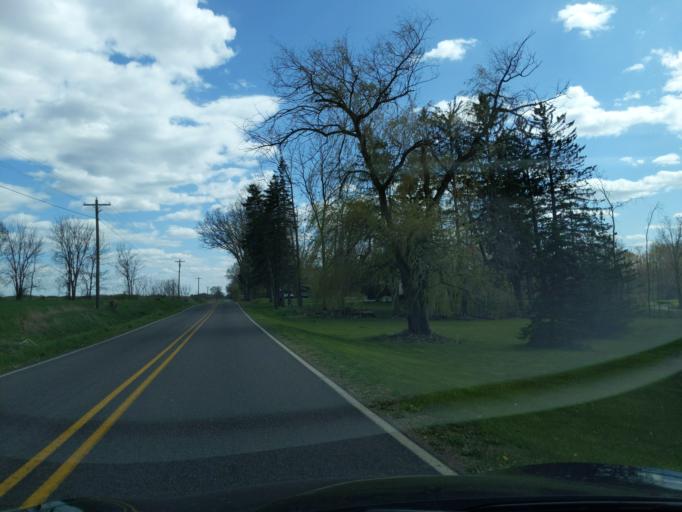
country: US
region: Michigan
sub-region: Ingham County
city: Leslie
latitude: 42.4126
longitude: -84.5416
